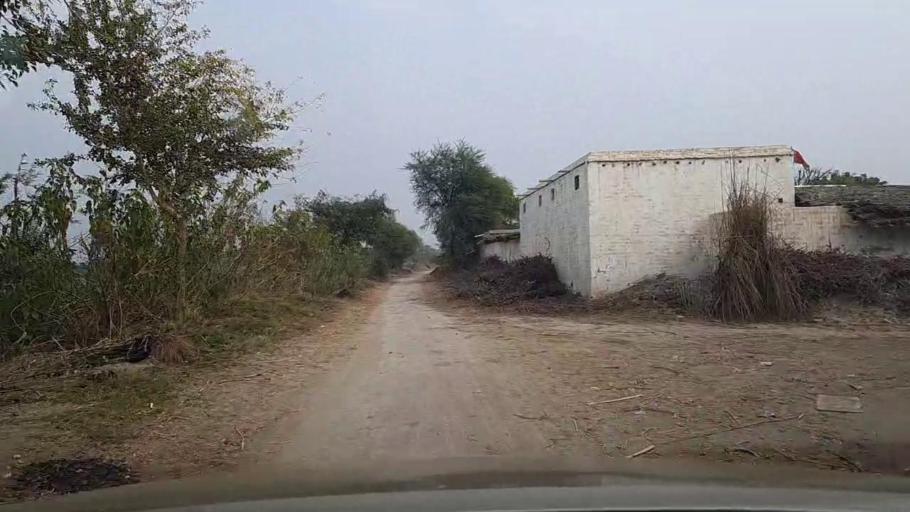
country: PK
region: Sindh
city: Sanghar
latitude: 26.1393
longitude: 68.9394
